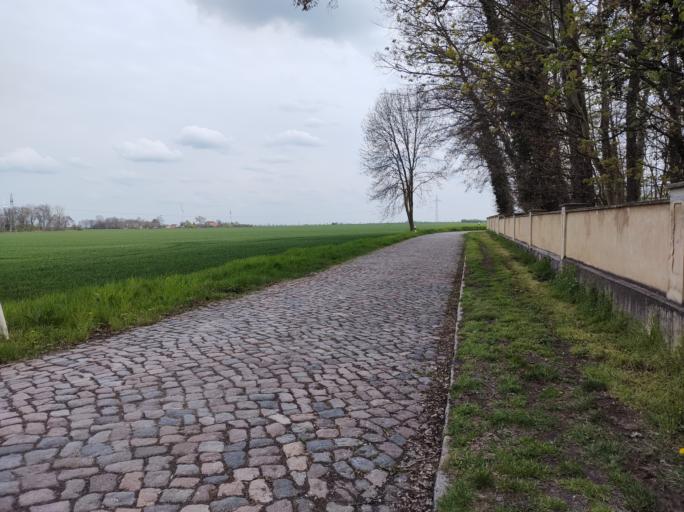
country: DE
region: Saxony-Anhalt
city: Niemberg
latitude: 51.5783
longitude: 12.1341
